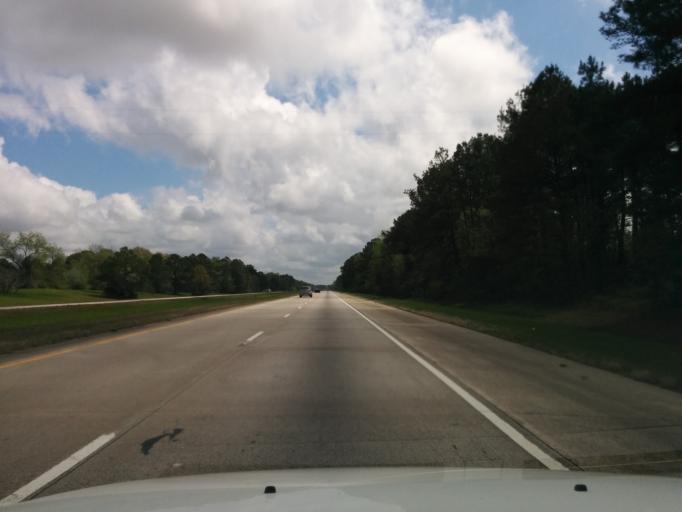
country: US
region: Georgia
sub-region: Bulloch County
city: Brooklet
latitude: 32.2694
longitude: -81.7452
